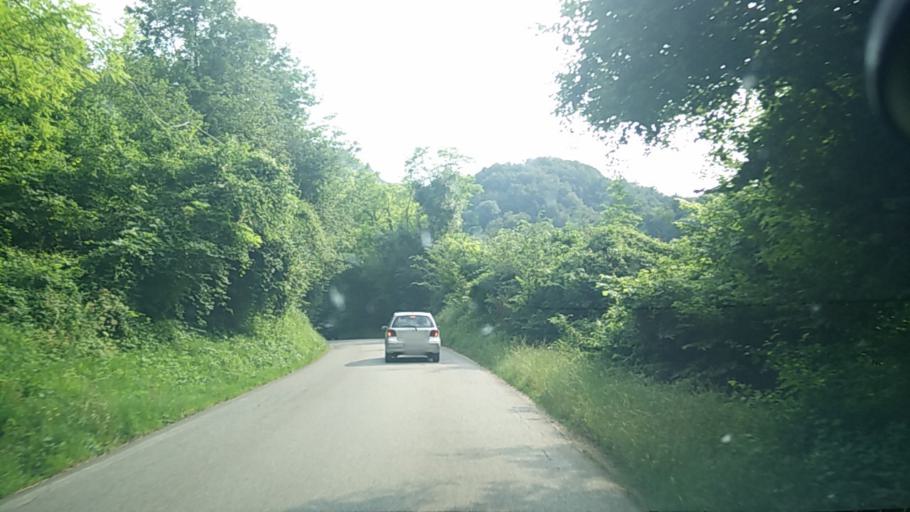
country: IT
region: Veneto
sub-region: Provincia di Treviso
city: Miane
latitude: 45.9107
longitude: 12.0772
